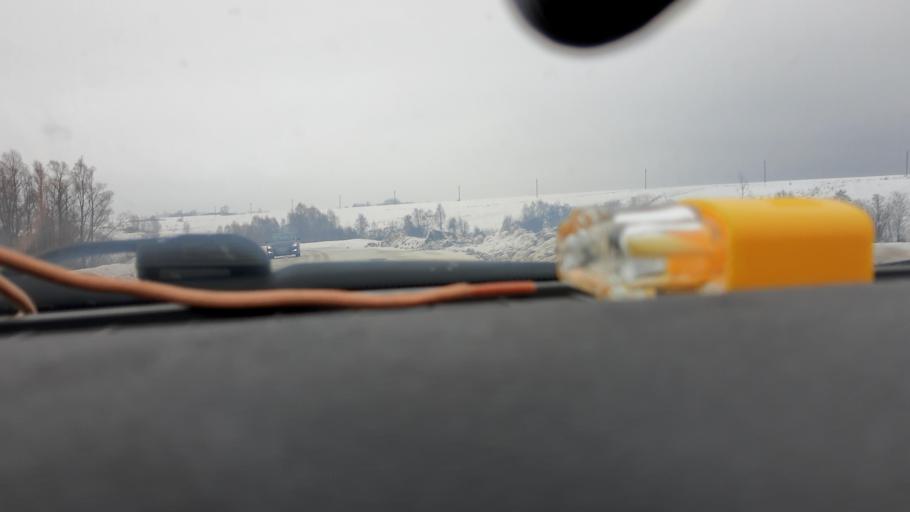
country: RU
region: Bashkortostan
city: Iglino
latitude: 54.6415
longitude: 56.4235
